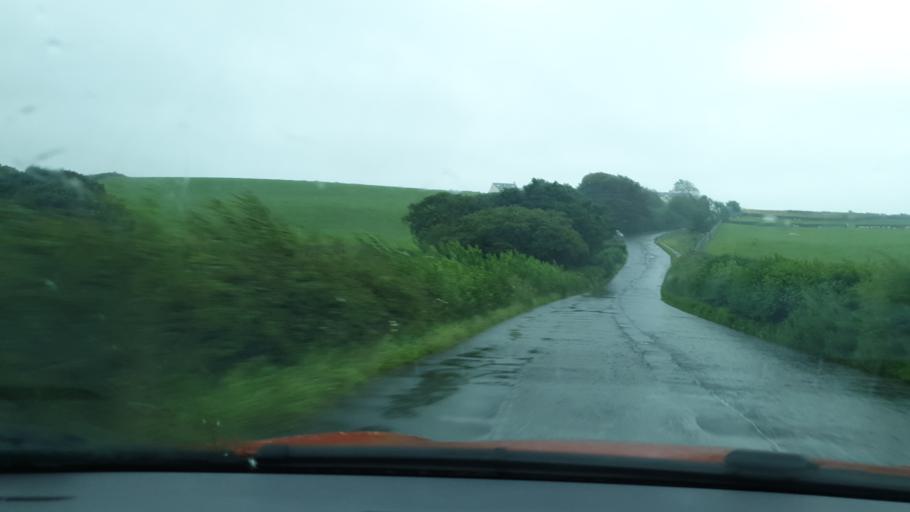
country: GB
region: England
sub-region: Cumbria
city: Millom
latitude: 54.2814
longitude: -3.2223
